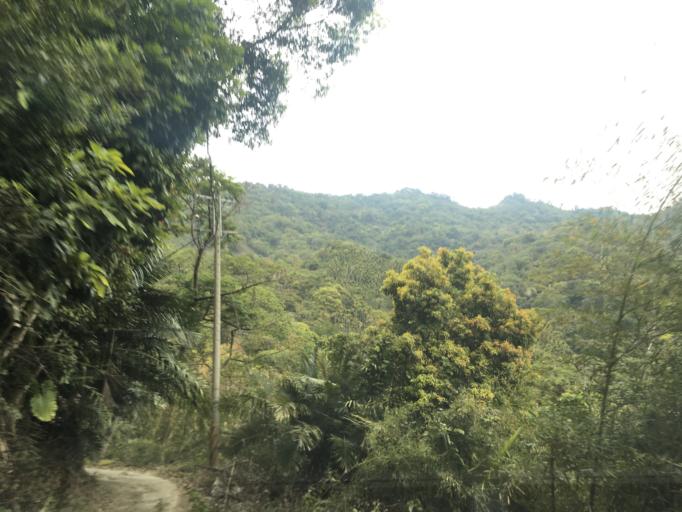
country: TW
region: Taiwan
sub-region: Taichung City
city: Taichung
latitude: 24.1329
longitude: 120.8246
